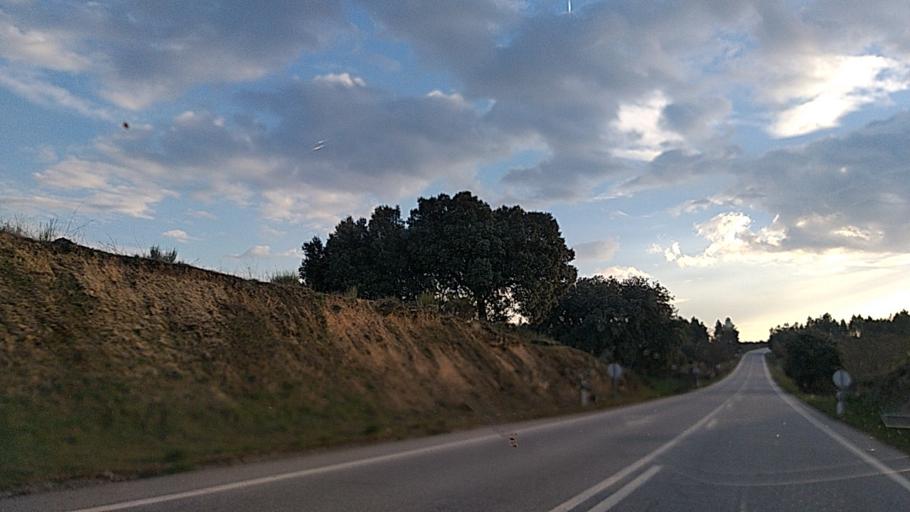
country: PT
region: Guarda
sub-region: Pinhel
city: Pinhel
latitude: 40.6730
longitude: -6.9516
